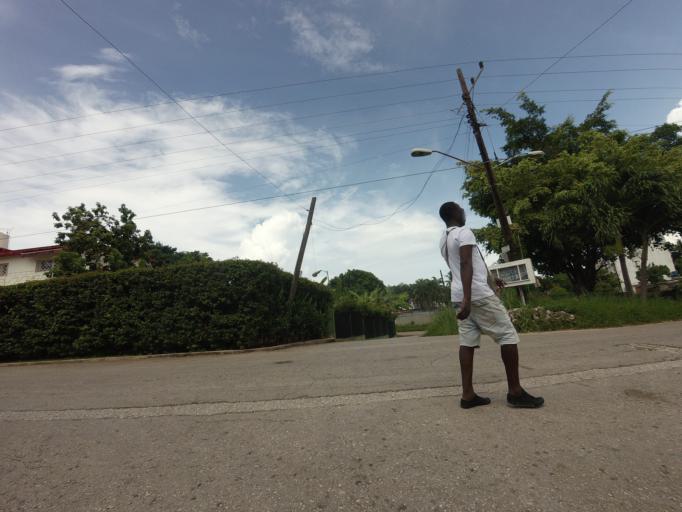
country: CU
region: La Habana
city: Cerro
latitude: 23.1009
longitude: -82.4432
